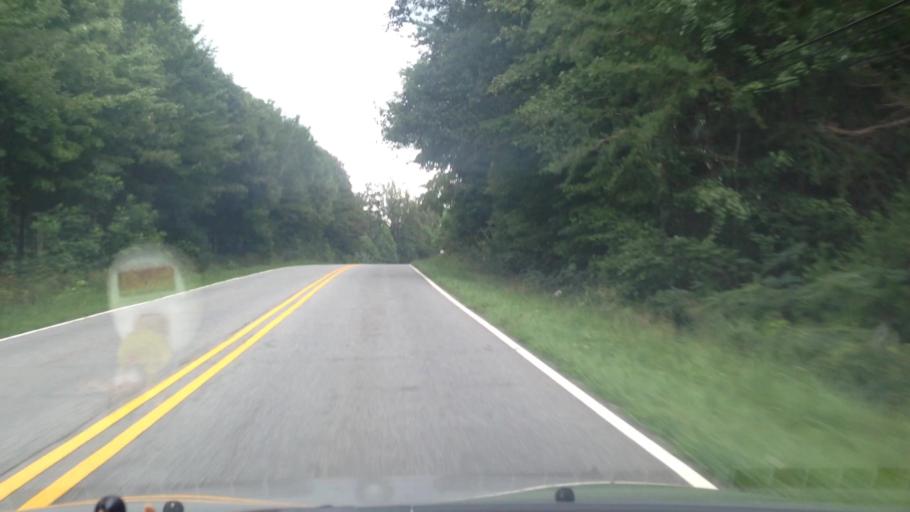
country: US
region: North Carolina
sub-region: Forsyth County
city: Walkertown
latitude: 36.2034
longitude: -80.1675
